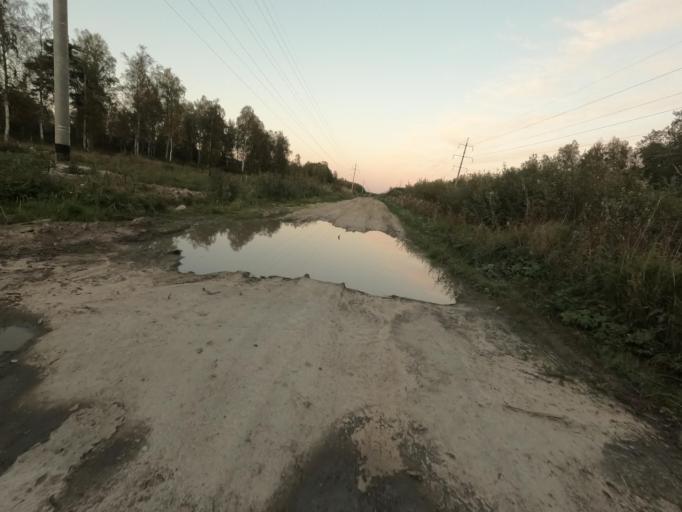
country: RU
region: Leningrad
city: Otradnoye
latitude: 59.7692
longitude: 30.8423
